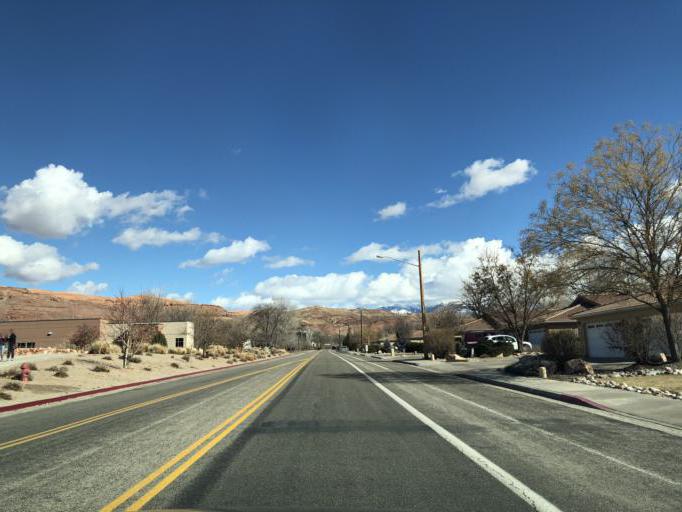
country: US
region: Utah
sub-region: Grand County
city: Moab
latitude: 38.5743
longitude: -109.5598
